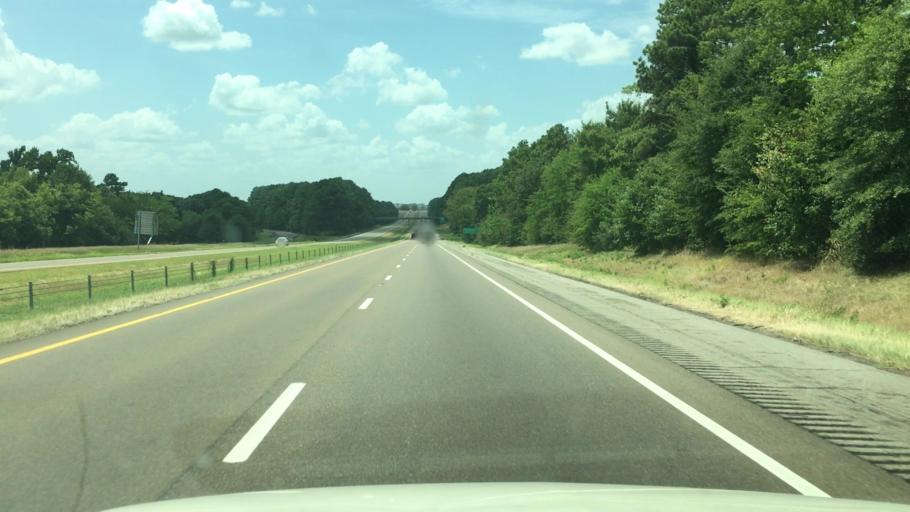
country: US
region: Texas
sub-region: Titus County
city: Mount Pleasant
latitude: 33.1912
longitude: -94.9373
